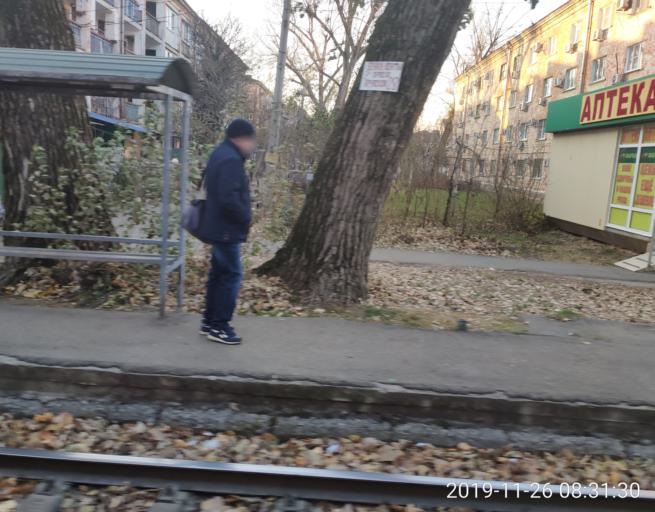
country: RU
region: Krasnodarskiy
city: Krasnodar
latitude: 45.0526
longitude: 38.9989
